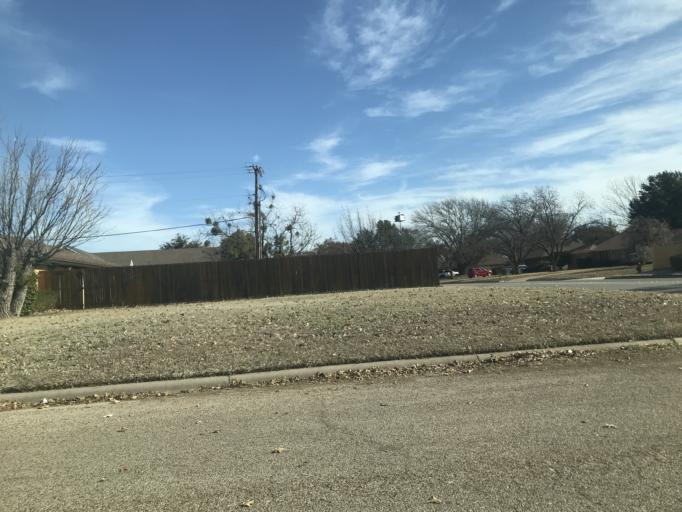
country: US
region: Texas
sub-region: Taylor County
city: Abilene
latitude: 32.4096
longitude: -99.7689
